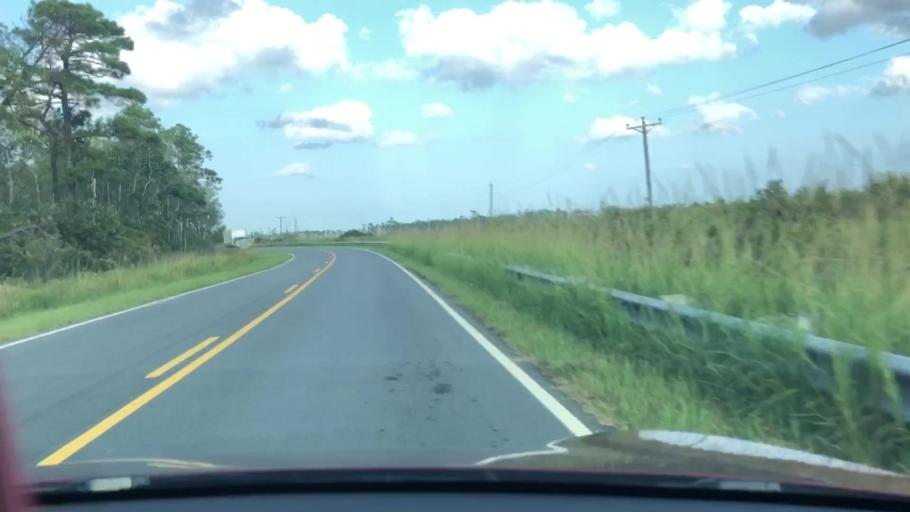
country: US
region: North Carolina
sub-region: Dare County
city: Wanchese
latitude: 35.6085
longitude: -75.8017
